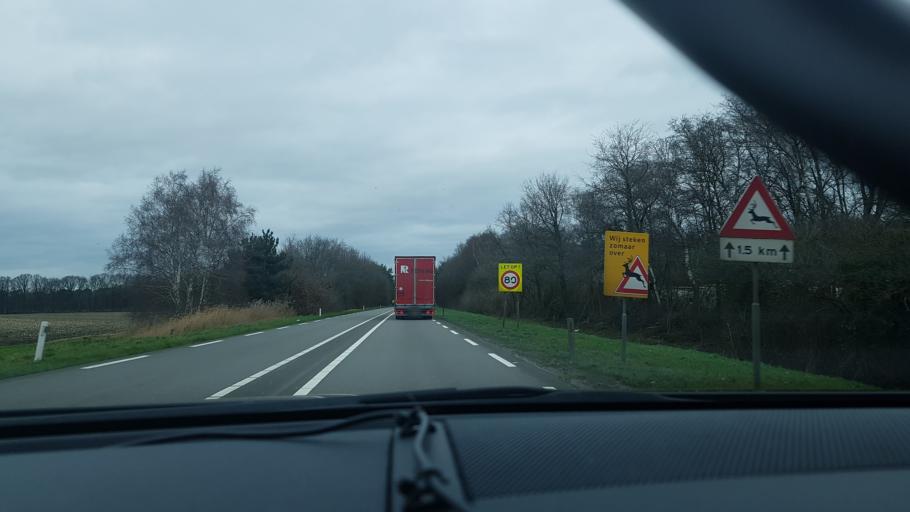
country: NL
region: North Brabant
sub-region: Gemeente Asten
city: Asten
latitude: 51.4560
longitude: 5.7208
